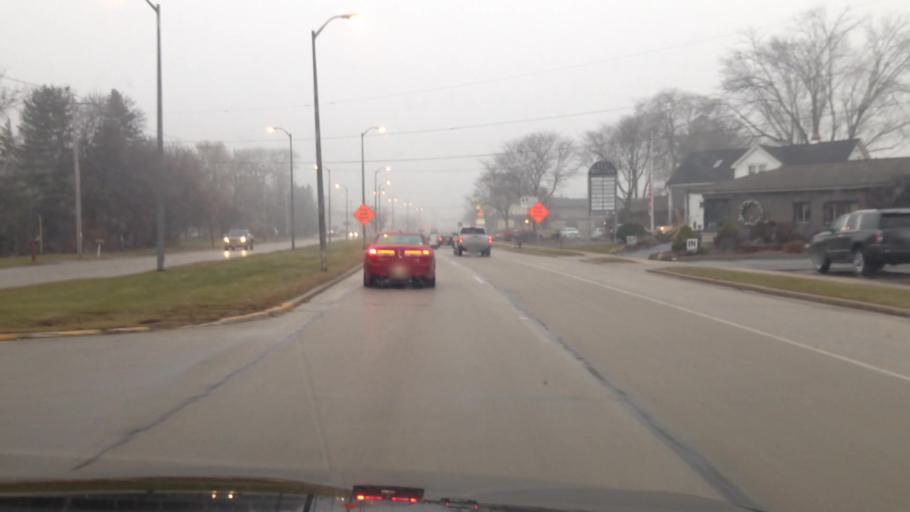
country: US
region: Wisconsin
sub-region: Milwaukee County
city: Hales Corners
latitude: 42.9408
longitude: -88.0418
